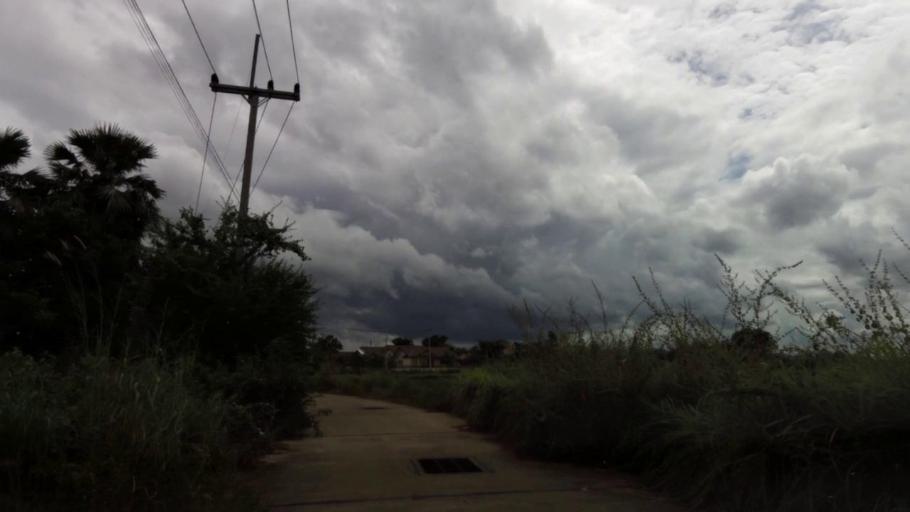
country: TH
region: Nakhon Sawan
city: Phai Sali
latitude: 15.5926
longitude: 100.6594
